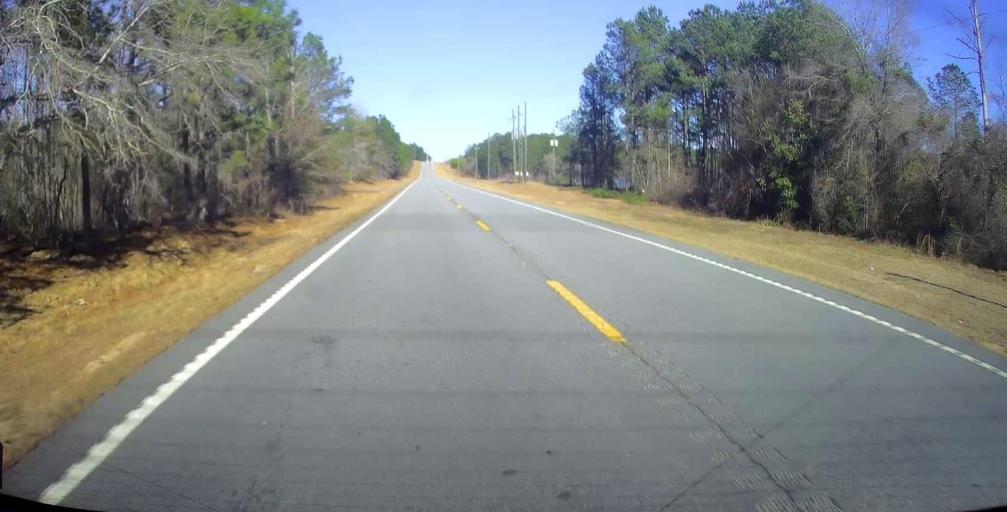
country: US
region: Georgia
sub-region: Taylor County
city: Butler
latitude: 32.5752
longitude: -84.2147
